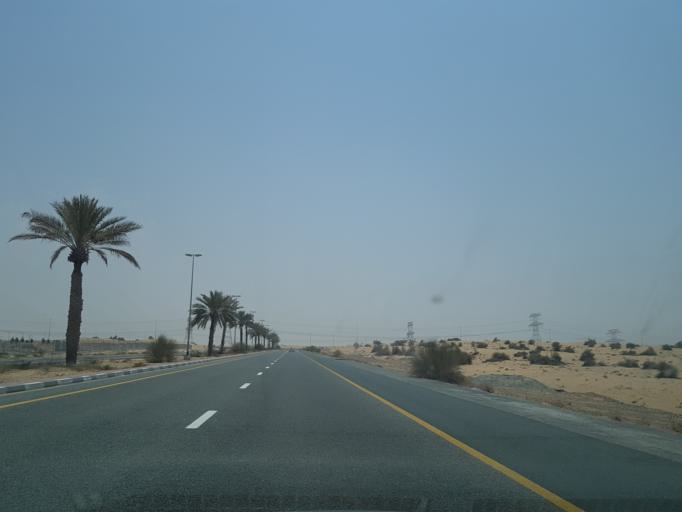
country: AE
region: Ash Shariqah
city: Sharjah
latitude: 25.1068
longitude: 55.4115
